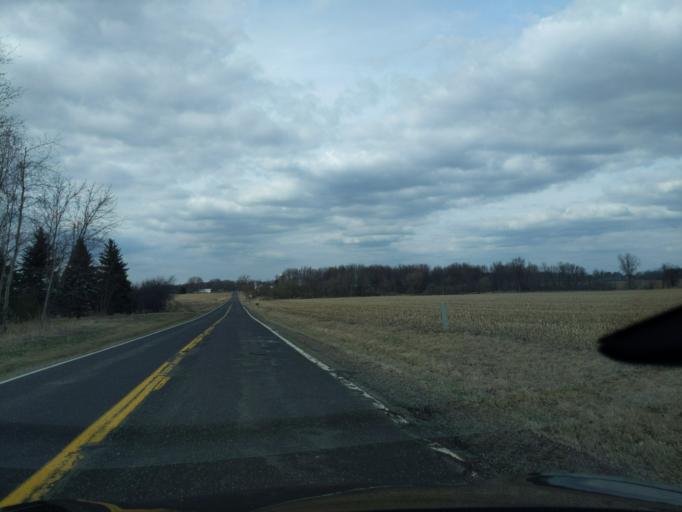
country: US
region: Michigan
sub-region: Ingham County
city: Mason
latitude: 42.5632
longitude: -84.4833
